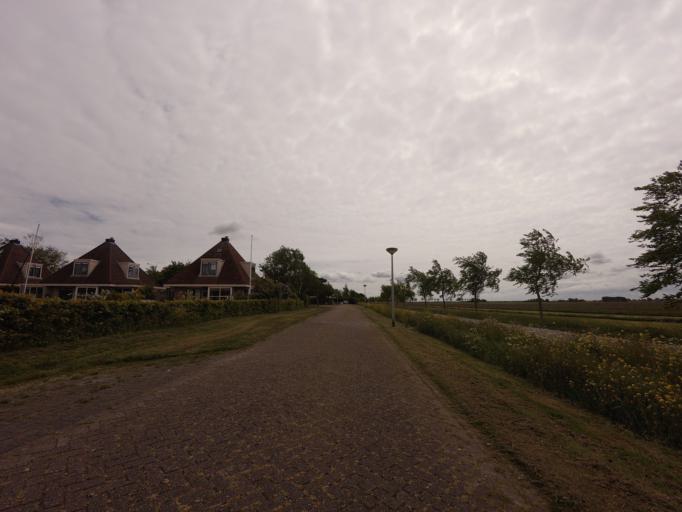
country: NL
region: Friesland
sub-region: Sudwest Fryslan
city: Woudsend
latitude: 52.9471
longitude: 5.6209
